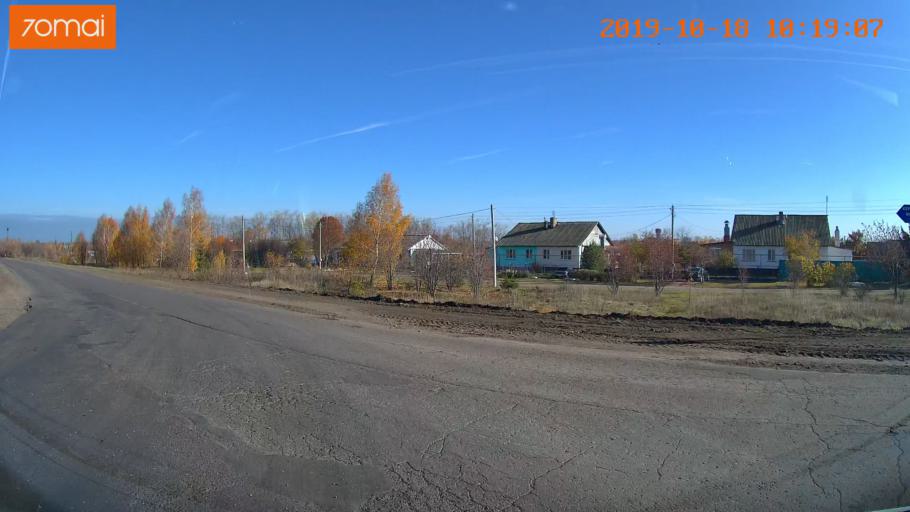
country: RU
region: Tula
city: Kurkino
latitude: 53.4195
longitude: 38.6457
